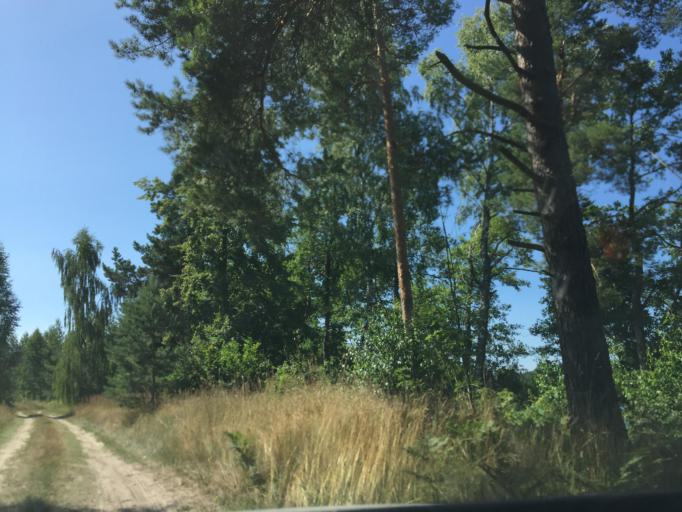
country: LV
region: Talsu Rajons
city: Stende
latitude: 57.1571
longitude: 22.3029
